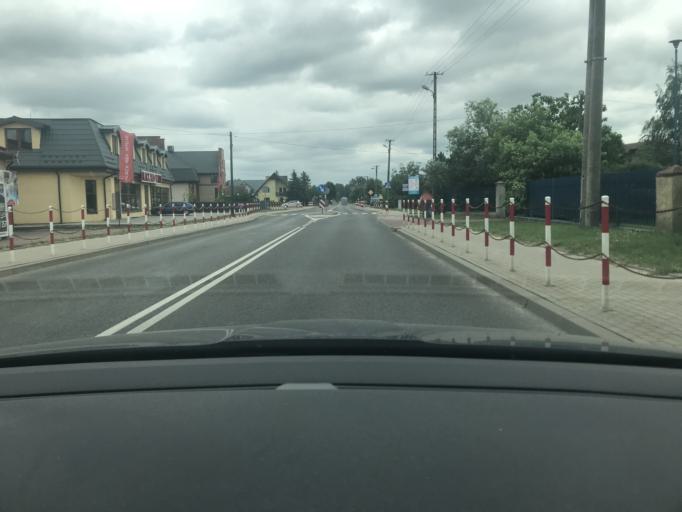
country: PL
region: Lodz Voivodeship
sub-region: Powiat poddebicki
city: Poddebice
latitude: 51.8930
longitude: 18.9620
